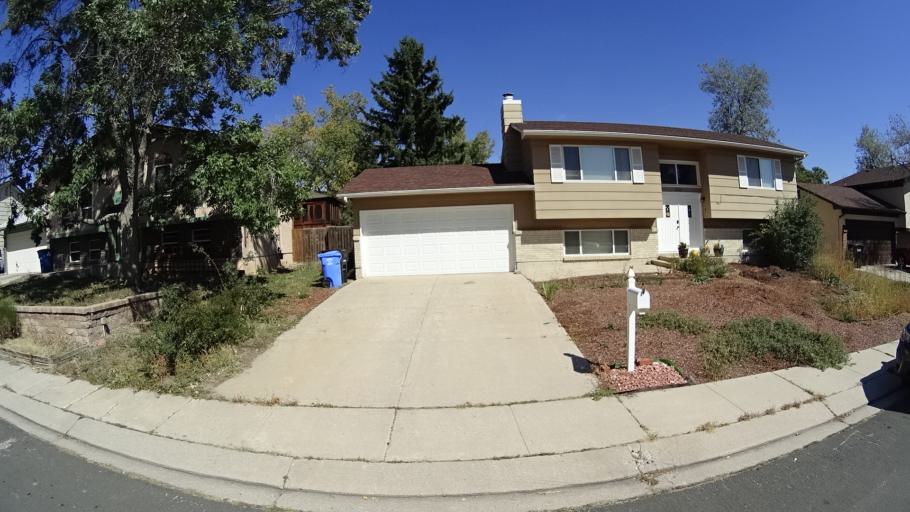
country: US
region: Colorado
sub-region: El Paso County
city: Cimarron Hills
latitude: 38.9067
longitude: -104.7659
